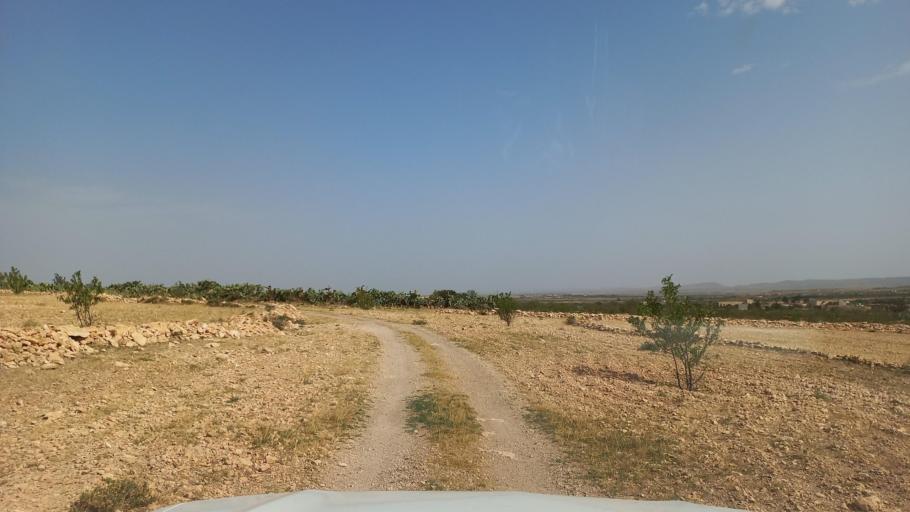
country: TN
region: Al Qasrayn
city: Kasserine
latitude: 35.2999
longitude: 8.9404
